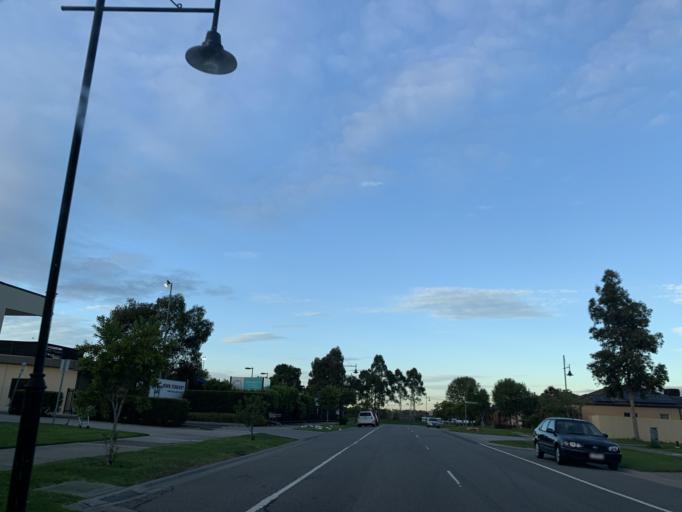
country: AU
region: Victoria
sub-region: Casey
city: Cranbourne North
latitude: -38.0847
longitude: 145.2909
